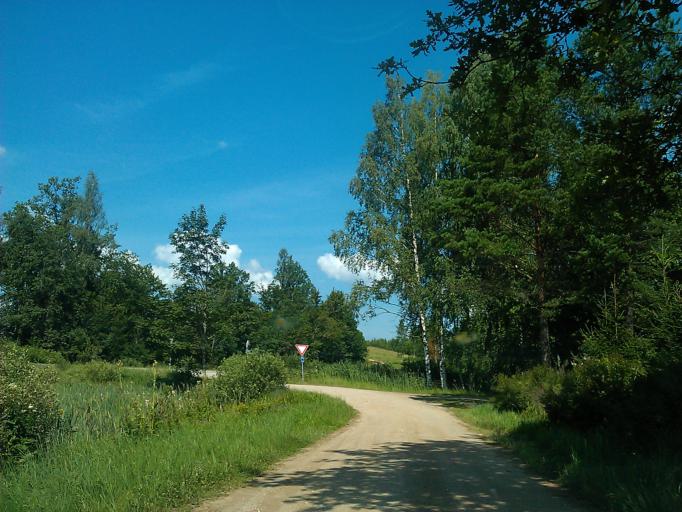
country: LV
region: Amatas Novads
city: Drabesi
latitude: 57.2497
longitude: 25.2614
